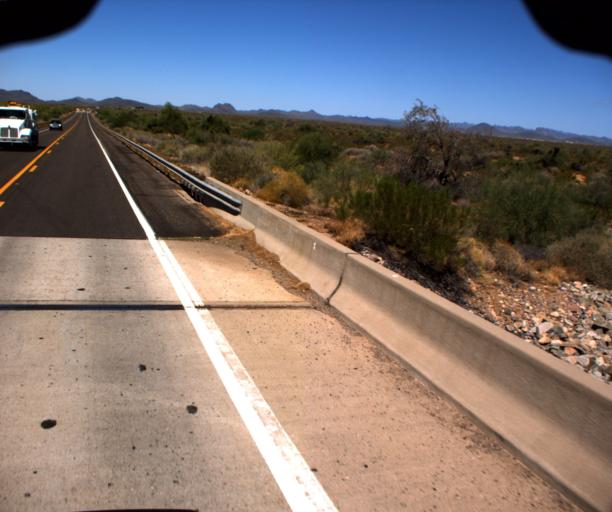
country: US
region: Arizona
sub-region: Maricopa County
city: Anthem
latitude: 33.7977
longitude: -112.2133
